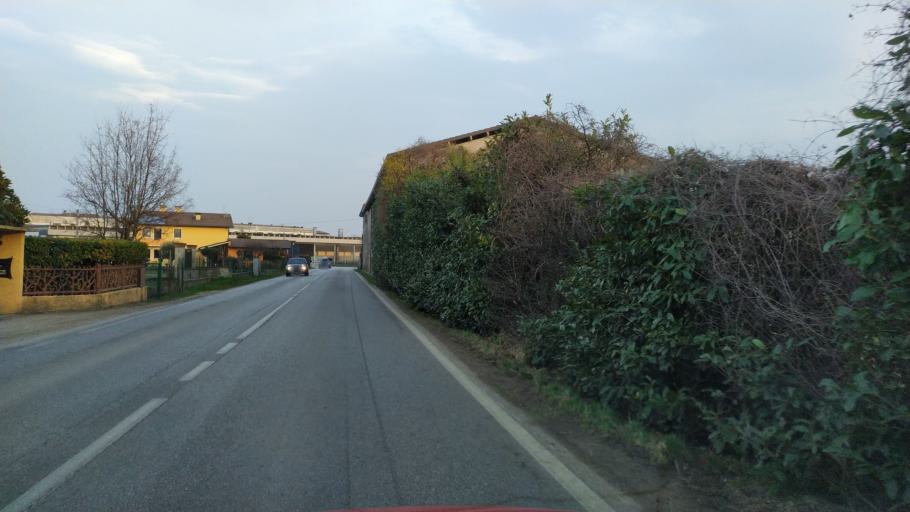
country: IT
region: Veneto
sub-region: Provincia di Vicenza
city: Preara-Moraro-Leva Nord
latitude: 45.6860
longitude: 11.5301
